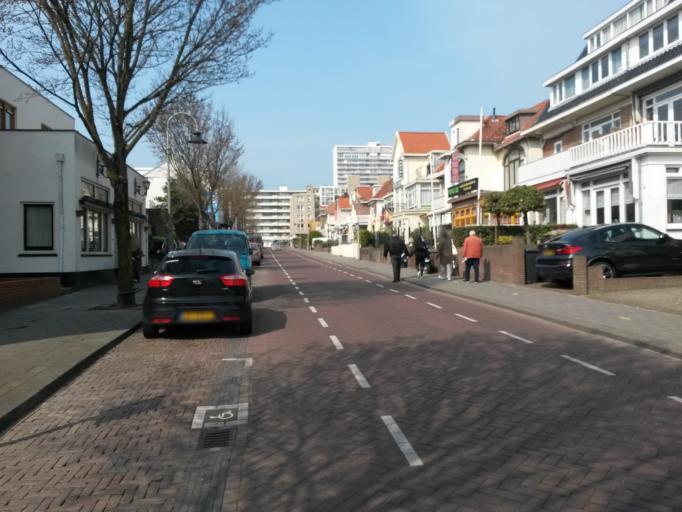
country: NL
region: North Holland
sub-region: Gemeente Zandvoort
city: Zandvoort
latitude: 52.3748
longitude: 4.5320
